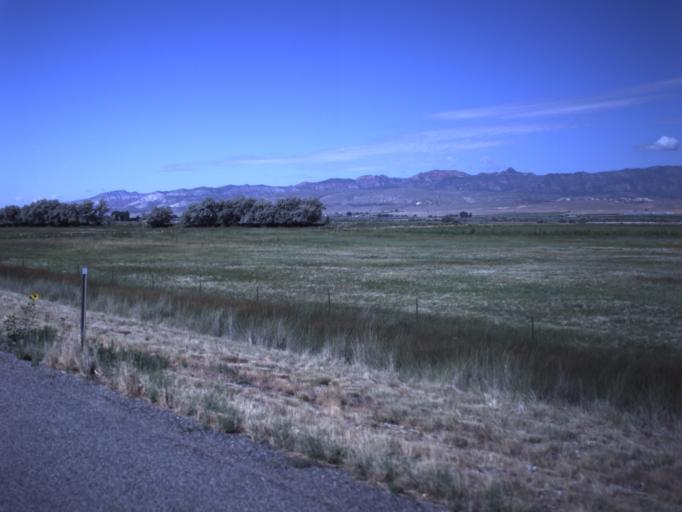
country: US
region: Utah
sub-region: Sevier County
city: Salina
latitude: 38.9829
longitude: -111.8524
